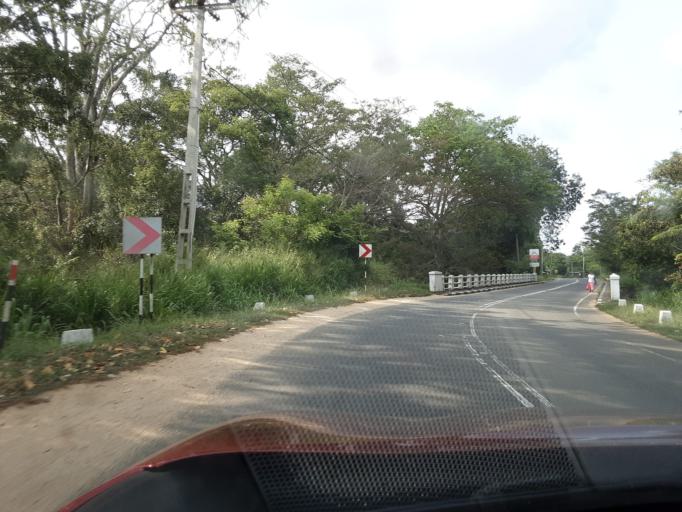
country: LK
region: Uva
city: Haputale
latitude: 6.5239
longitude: 81.1239
